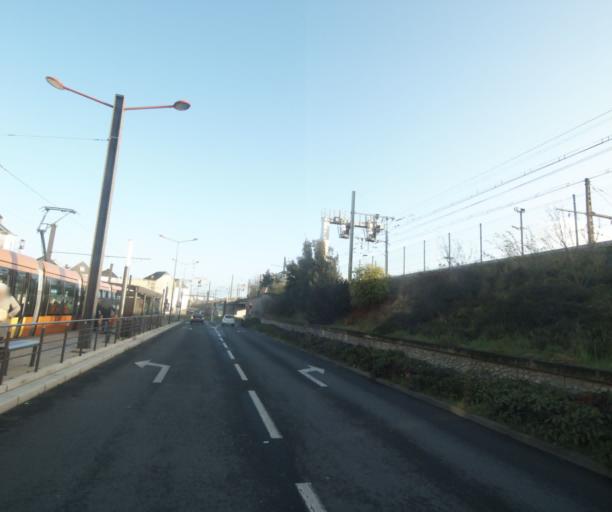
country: FR
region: Pays de la Loire
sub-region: Departement de la Sarthe
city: Le Mans
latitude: 47.9927
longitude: 0.2036
